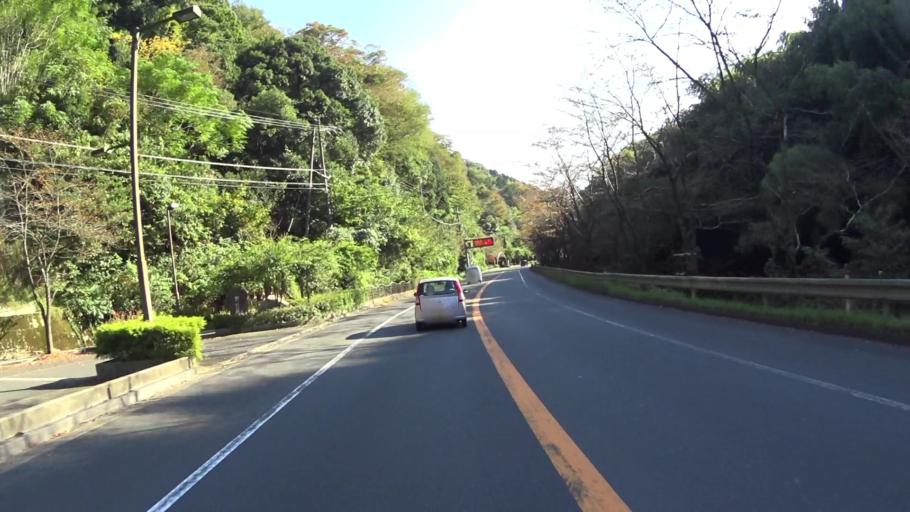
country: JP
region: Kyoto
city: Miyazu
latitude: 35.5454
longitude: 135.1109
